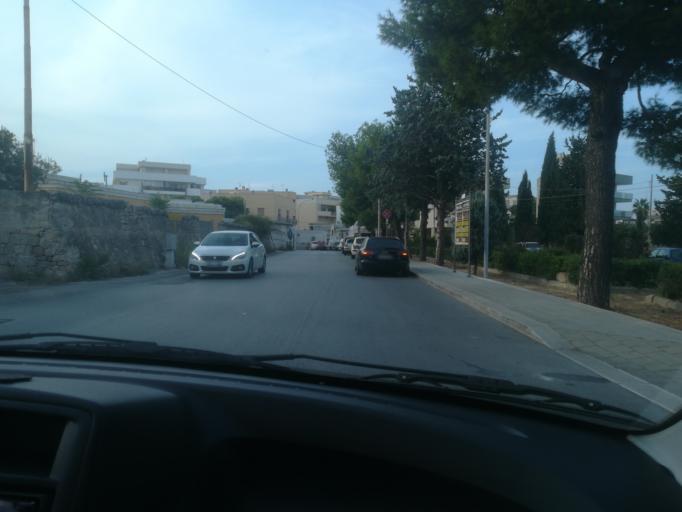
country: IT
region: Apulia
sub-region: Provincia di Bari
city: Monopoli
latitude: 40.9446
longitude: 17.2997
